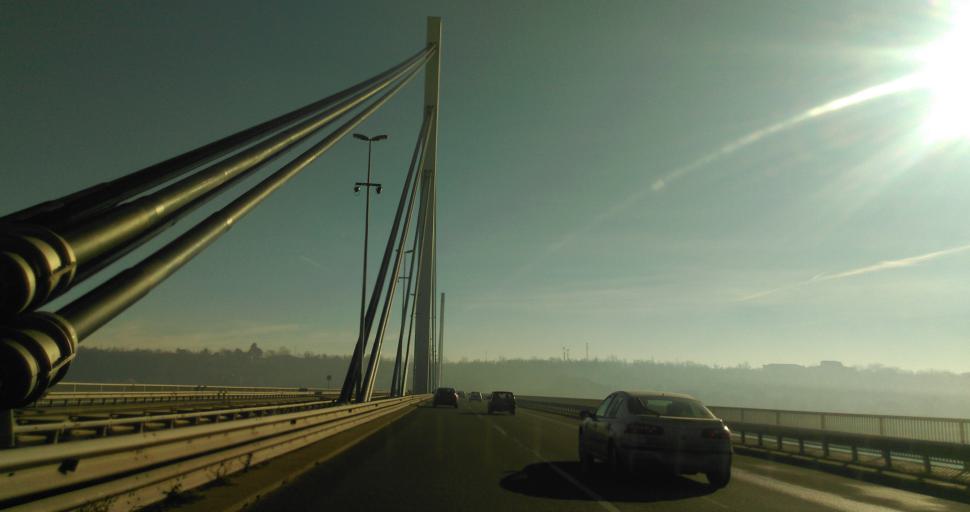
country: RS
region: Autonomna Pokrajina Vojvodina
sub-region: Juznobacki Okrug
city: Novi Sad
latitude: 45.2353
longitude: 19.8476
